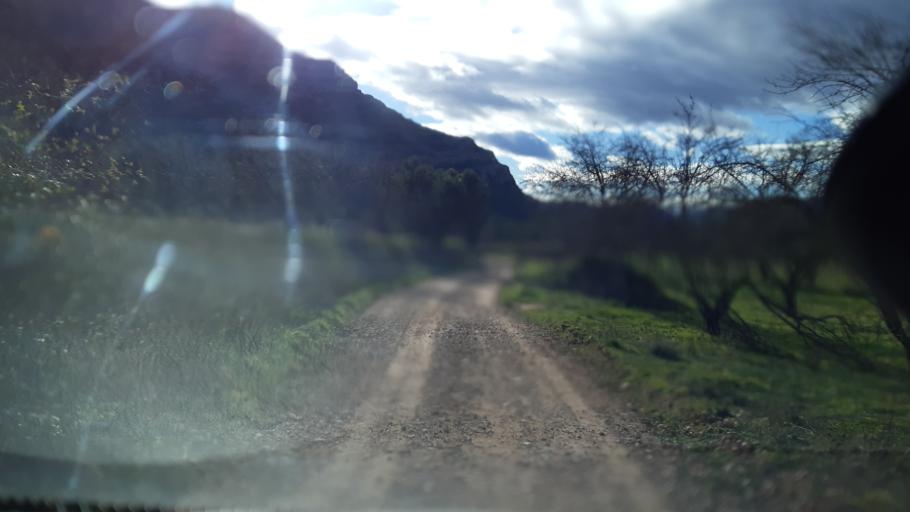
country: ES
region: Aragon
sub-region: Provincia de Teruel
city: Valderrobres
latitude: 40.8568
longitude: 0.2330
